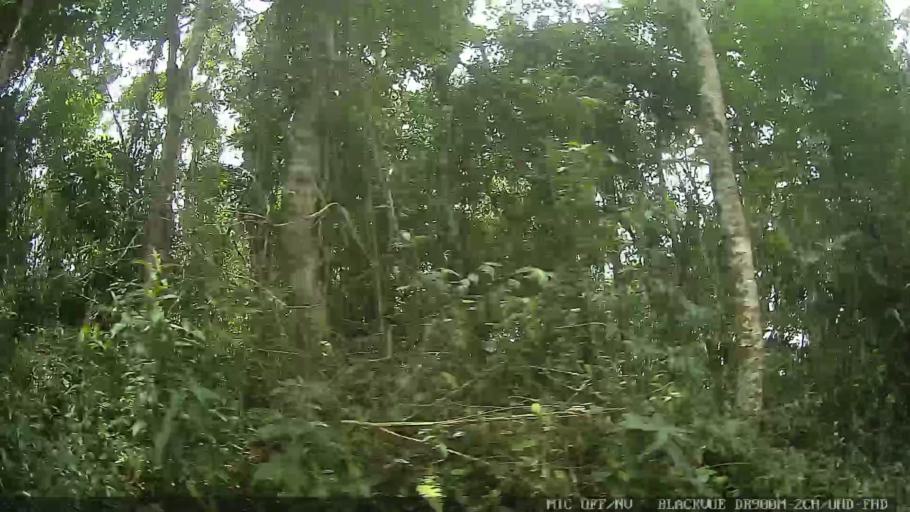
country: BR
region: Sao Paulo
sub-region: Mogi das Cruzes
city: Mogi das Cruzes
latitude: -23.5035
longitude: -46.2035
